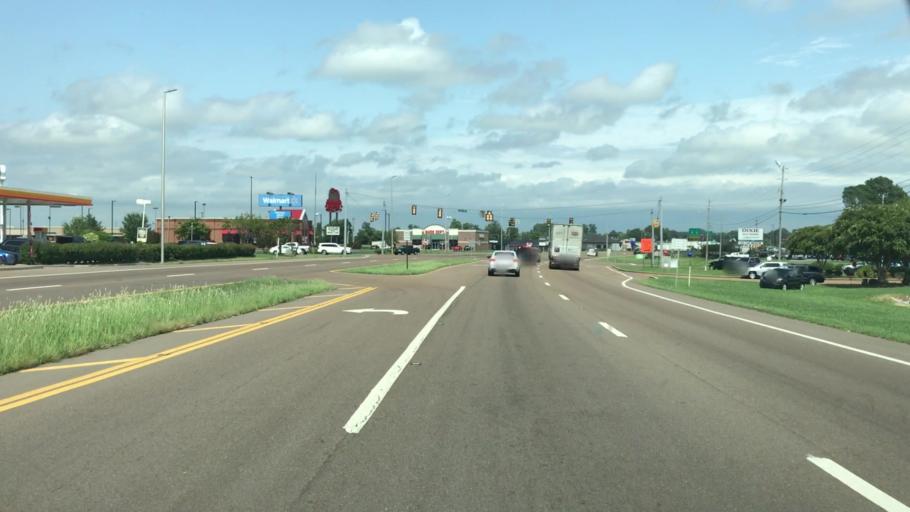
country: US
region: Tennessee
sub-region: Obion County
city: Union City
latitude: 36.4128
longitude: -89.0775
